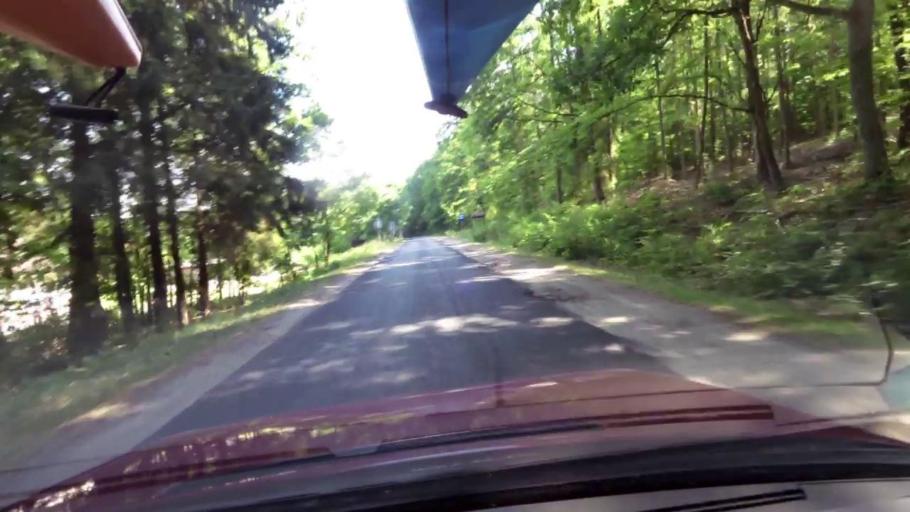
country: PL
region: Pomeranian Voivodeship
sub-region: Powiat slupski
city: Kepice
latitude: 54.1246
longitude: 16.9422
